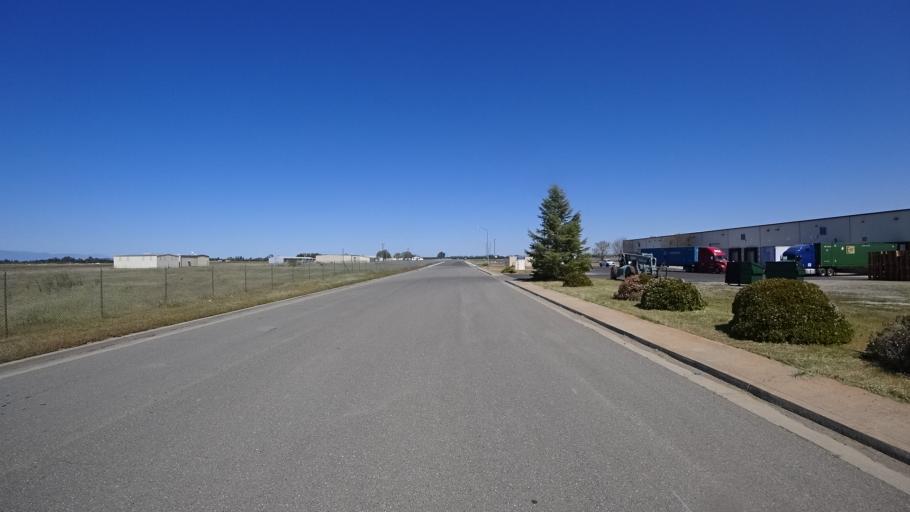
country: US
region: California
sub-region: Glenn County
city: Orland
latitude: 39.7183
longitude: -122.1432
